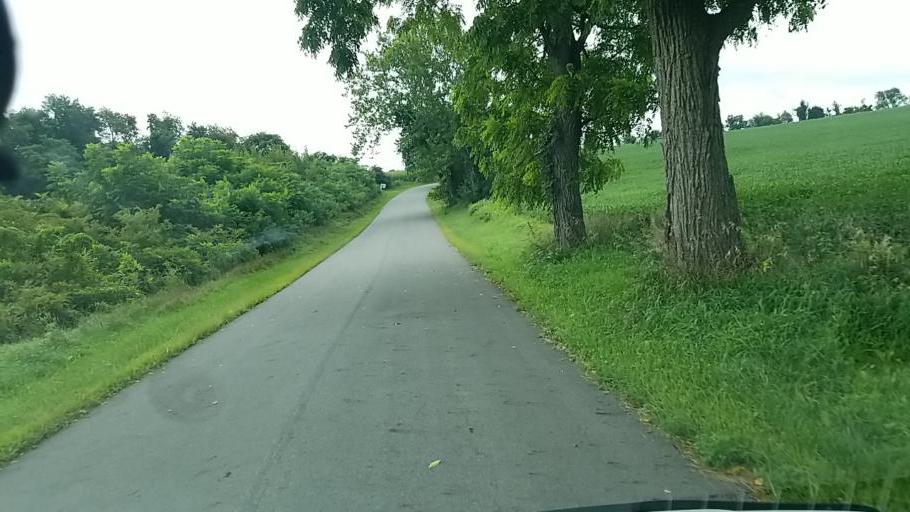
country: US
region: Pennsylvania
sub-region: Dauphin County
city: Elizabethville
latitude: 40.5175
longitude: -76.8846
